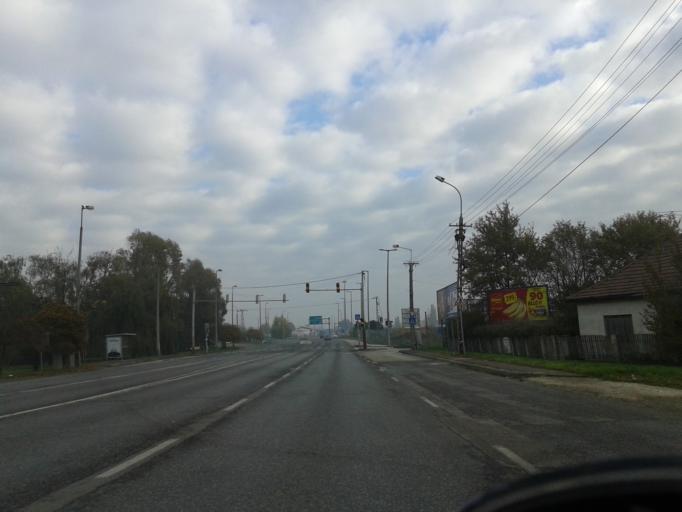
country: HU
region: Pest
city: Erd
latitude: 47.3786
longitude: 18.9322
